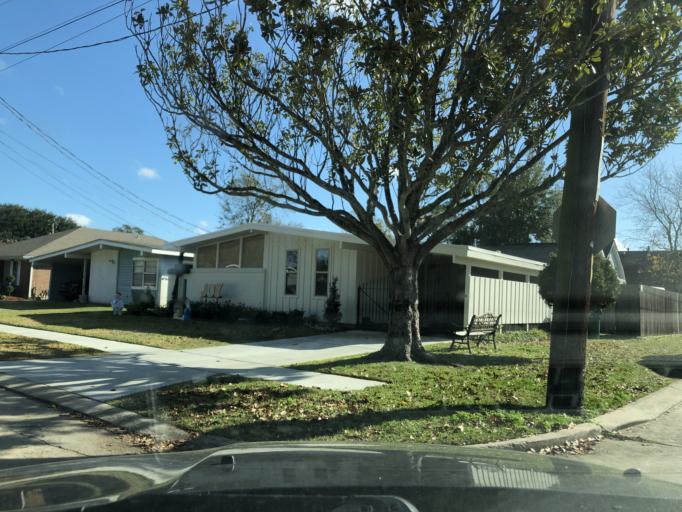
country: US
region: Louisiana
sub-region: Jefferson Parish
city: Metairie Terrace
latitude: 29.9862
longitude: -90.1613
